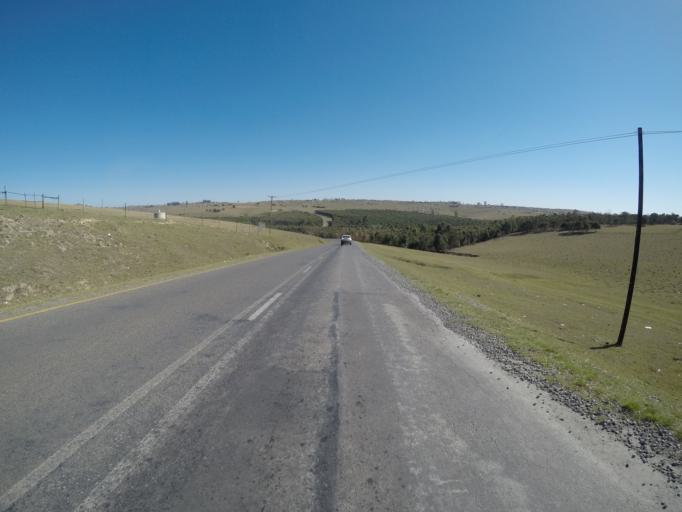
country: ZA
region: Eastern Cape
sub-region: OR Tambo District Municipality
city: Mthatha
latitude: -31.7809
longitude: 28.7382
